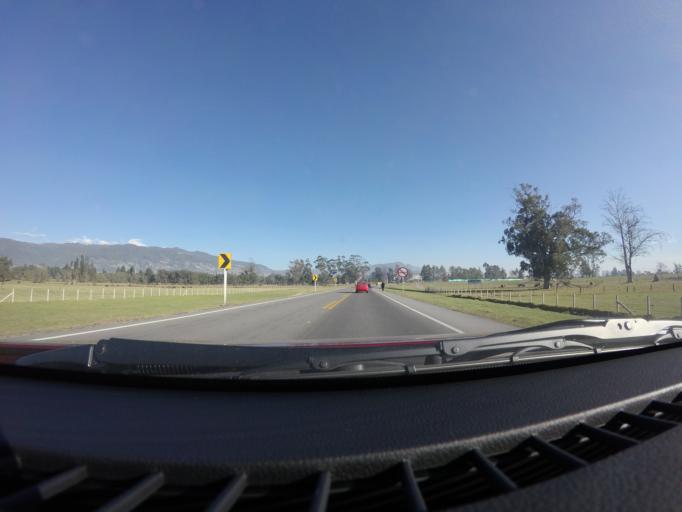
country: CO
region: Cundinamarca
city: Cogua
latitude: 5.0374
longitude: -73.9718
